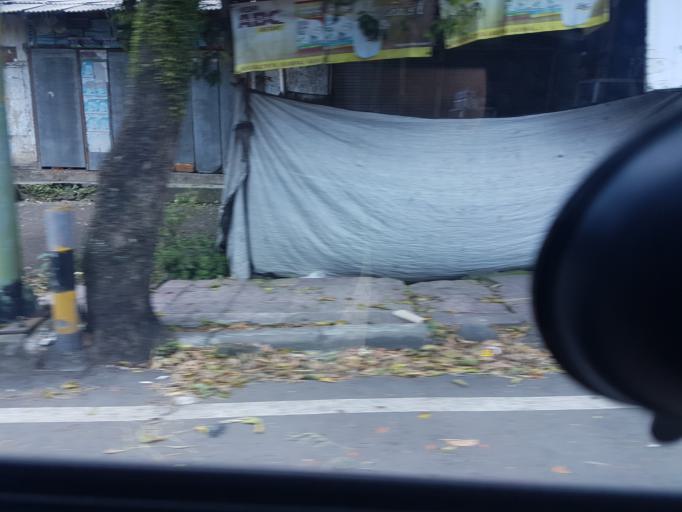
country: ID
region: Bali
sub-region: Kabupaten Gianyar
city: Ubud
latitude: -8.5150
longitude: 115.2935
